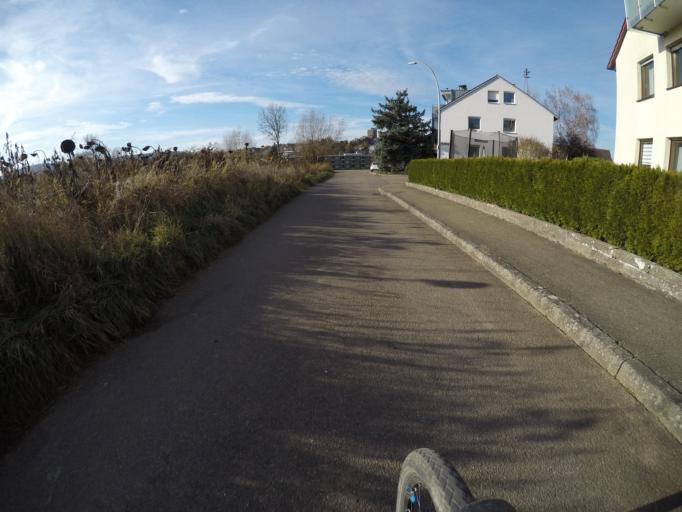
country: DE
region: Baden-Wuerttemberg
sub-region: Regierungsbezirk Stuttgart
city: Weinstadt-Endersbach
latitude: 48.8079
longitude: 9.3620
